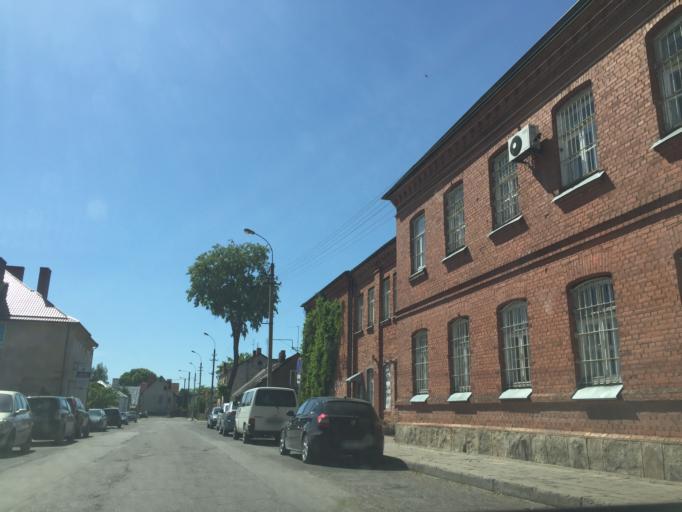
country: LT
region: Panevezys
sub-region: Panevezys City
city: Panevezys
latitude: 55.7332
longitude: 24.3547
